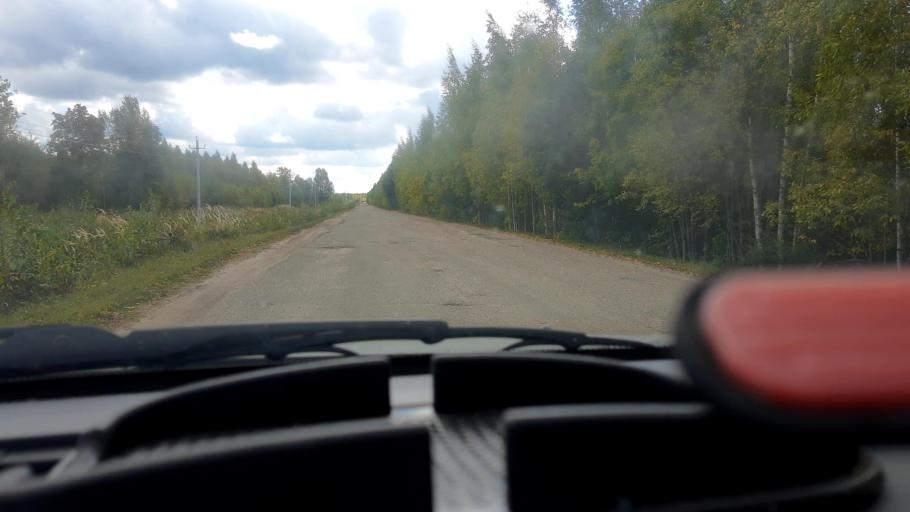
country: RU
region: Mariy-El
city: Kilemary
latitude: 56.8927
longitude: 46.7535
